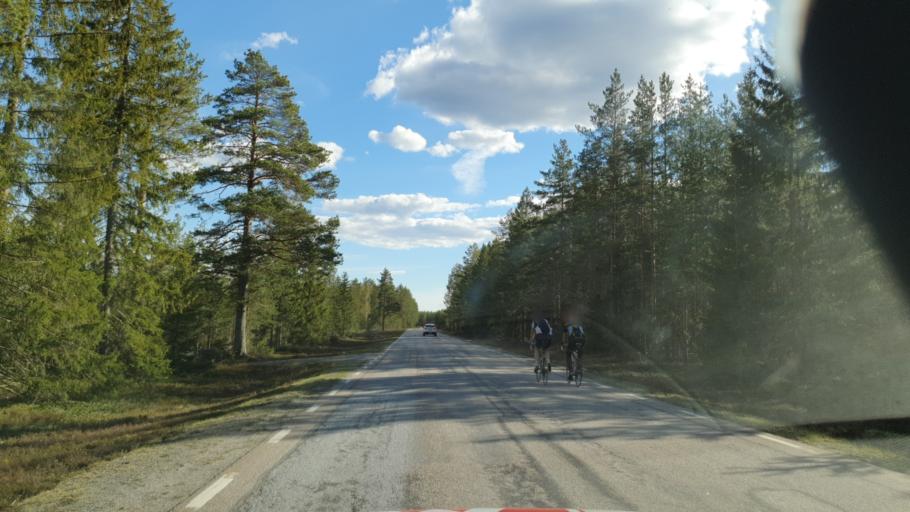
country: SE
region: Vaesterbotten
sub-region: Umea Kommun
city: Roback
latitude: 63.8727
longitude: 20.1501
